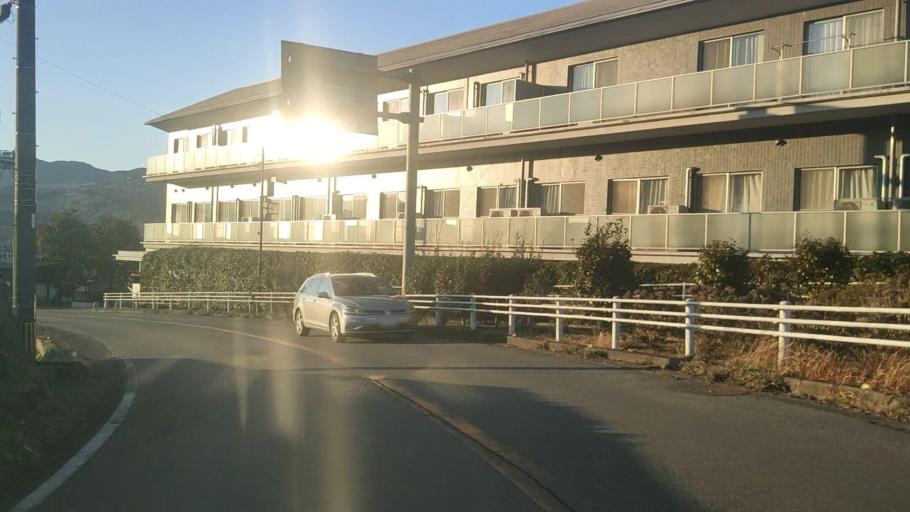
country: JP
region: Oita
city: Beppu
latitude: 33.2567
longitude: 131.3592
